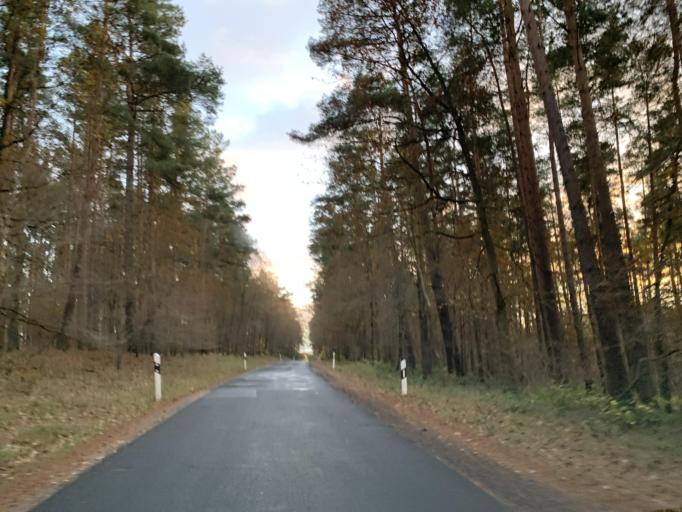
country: DE
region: Mecklenburg-Vorpommern
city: Blankensee
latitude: 53.3915
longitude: 13.2633
